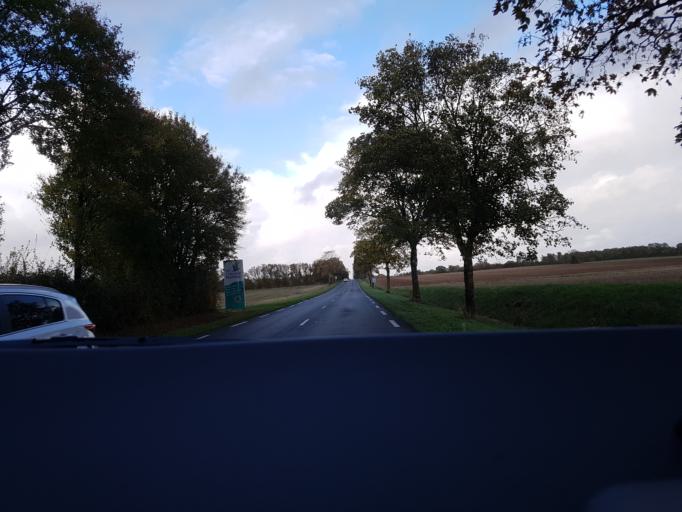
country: FR
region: Poitou-Charentes
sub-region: Departement de la Charente-Maritime
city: Aulnay
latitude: 46.0726
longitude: -0.3089
